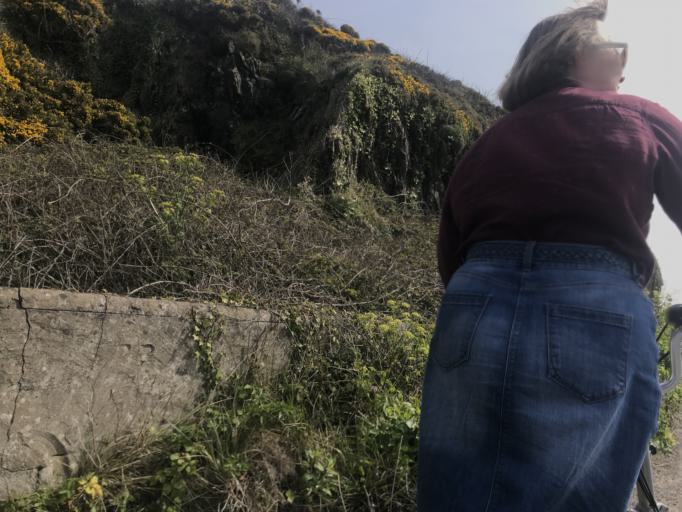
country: GB
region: England
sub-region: Devon
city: Braunton
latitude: 51.1225
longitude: -4.2405
